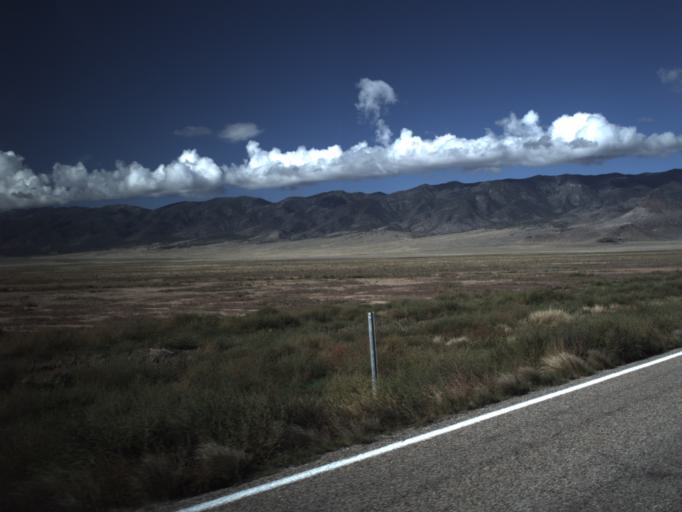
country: US
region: Utah
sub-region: Beaver County
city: Milford
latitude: 38.4676
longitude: -113.3981
